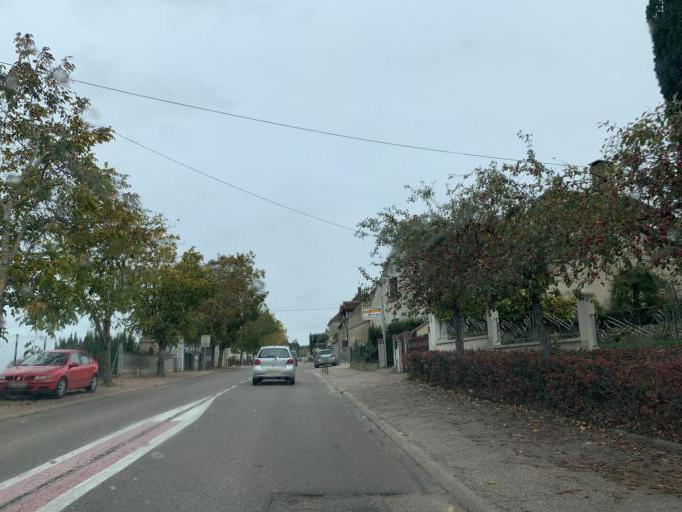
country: FR
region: Bourgogne
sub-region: Departement de l'Yonne
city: Moneteau
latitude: 47.8262
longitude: 3.5884
